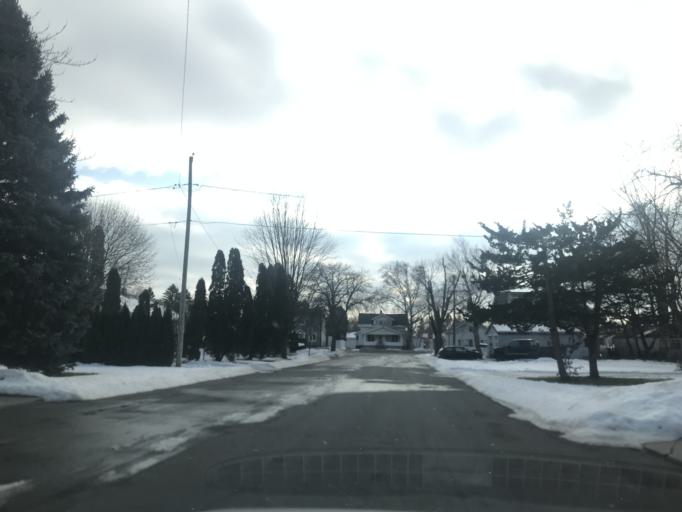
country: US
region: Wisconsin
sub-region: Marinette County
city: Marinette
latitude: 45.1000
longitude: -87.6490
